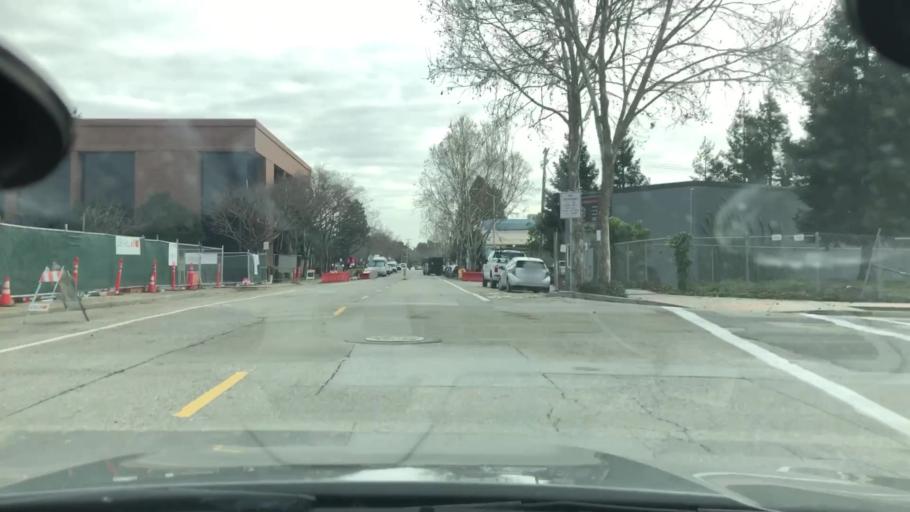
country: US
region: California
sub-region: Santa Clara County
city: Palo Alto
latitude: 37.4254
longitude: -122.1375
